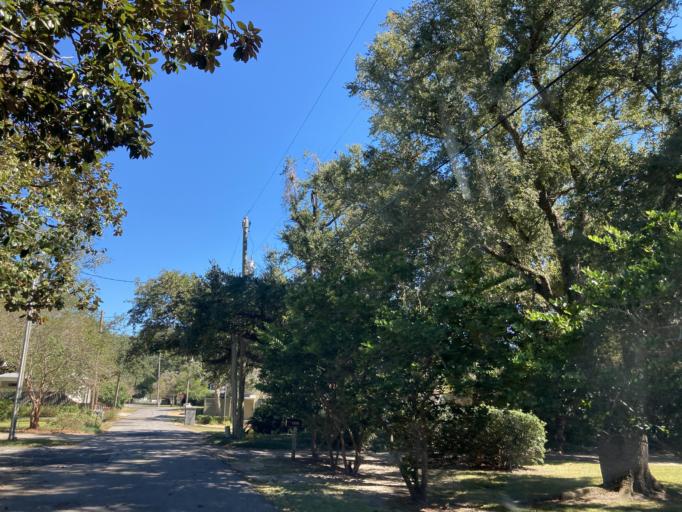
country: US
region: Mississippi
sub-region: Jackson County
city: Ocean Springs
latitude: 30.4074
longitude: -88.8235
